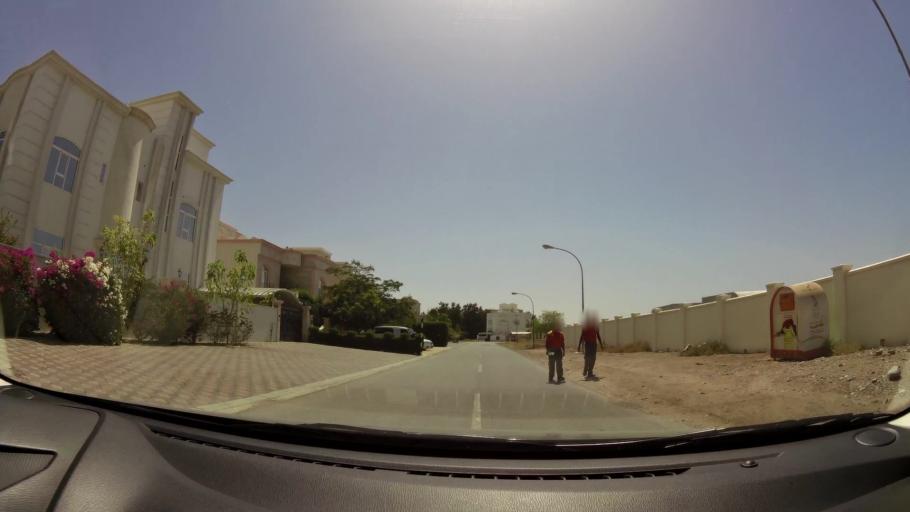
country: OM
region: Muhafazat Masqat
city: Bawshar
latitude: 23.6007
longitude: 58.3575
